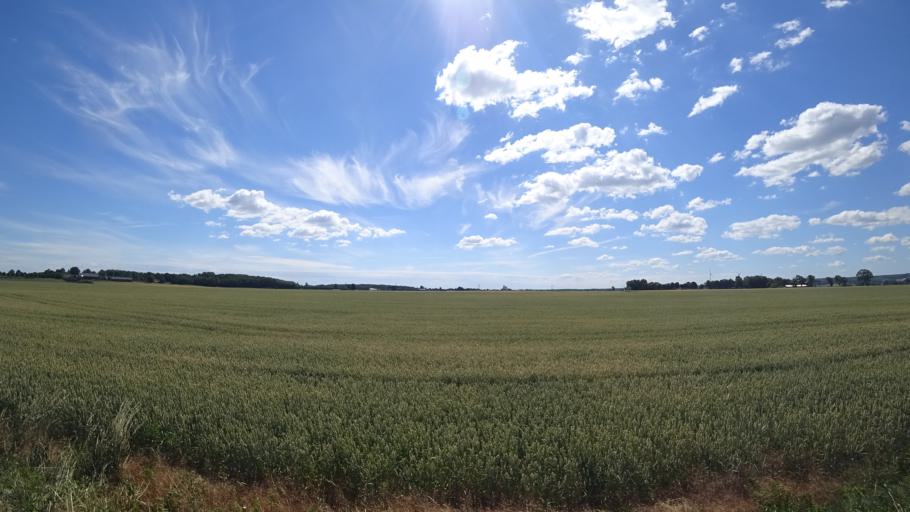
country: SE
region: Skane
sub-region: Kristianstads Kommun
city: Onnestad
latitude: 56.0705
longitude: 14.0690
